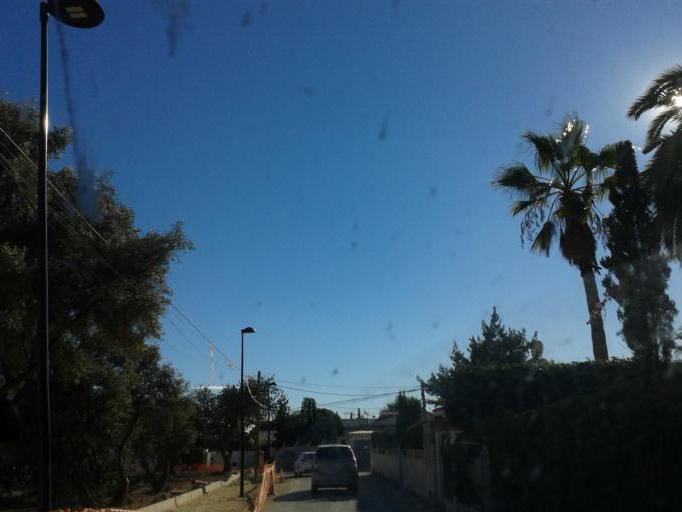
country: ES
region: Valencia
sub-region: Provincia de Alicante
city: el Campello
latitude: 38.4127
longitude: -0.4112
